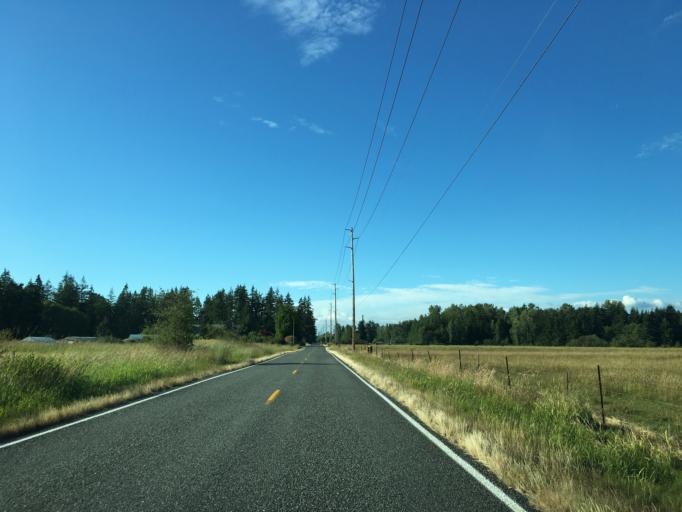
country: US
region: Washington
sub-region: Whatcom County
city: Birch Bay
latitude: 48.9242
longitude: -122.7044
